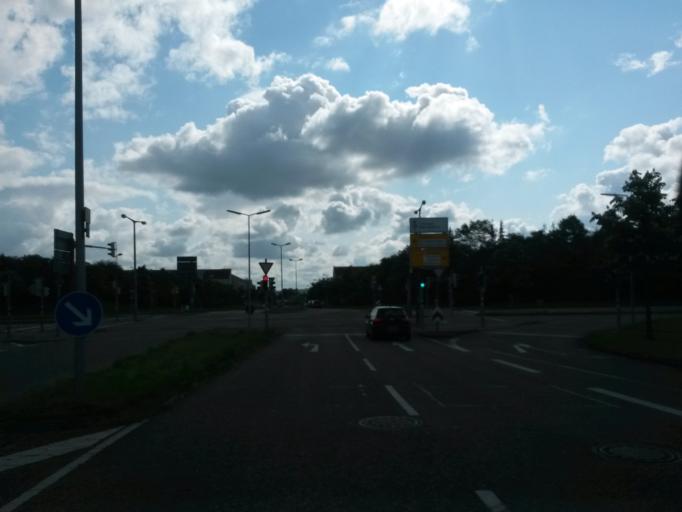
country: DE
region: Baden-Wuerttemberg
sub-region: Karlsruhe Region
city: Karlsruhe
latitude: 49.0348
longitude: 8.4504
